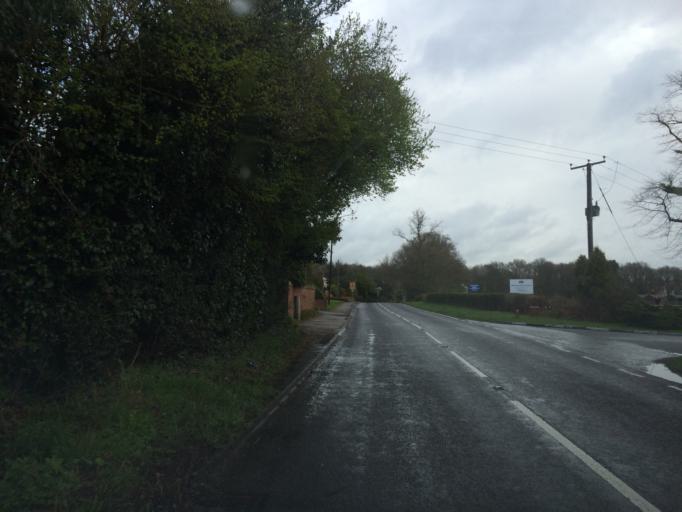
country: GB
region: England
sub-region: Surrey
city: Chobham
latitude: 51.3360
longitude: -0.6105
